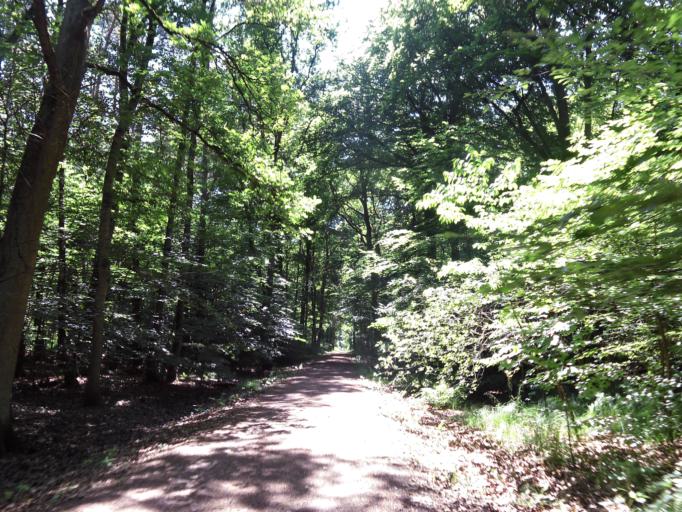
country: DE
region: Hesse
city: Langen
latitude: 49.9983
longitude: 8.6346
